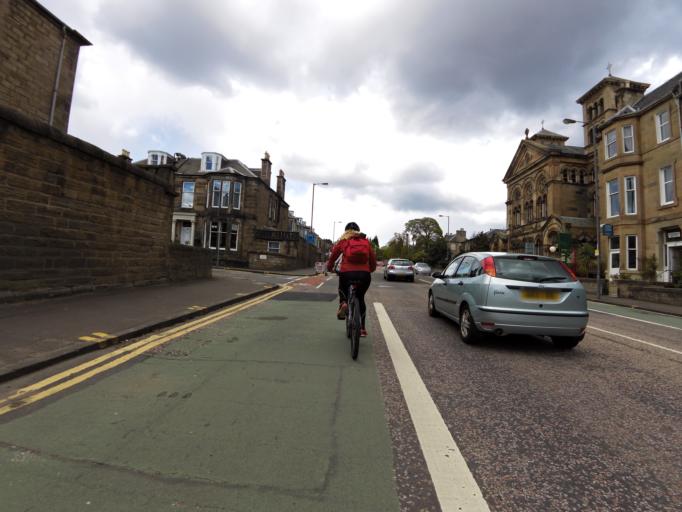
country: GB
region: Scotland
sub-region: Edinburgh
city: Edinburgh
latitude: 55.9359
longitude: -3.1697
